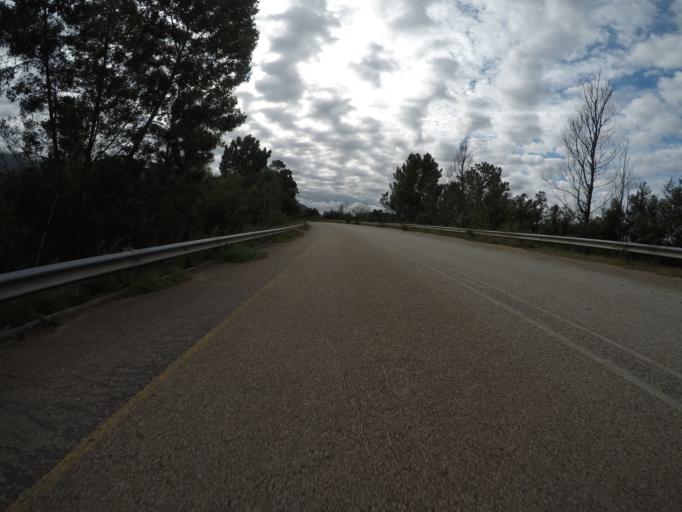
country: ZA
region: Eastern Cape
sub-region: Cacadu District Municipality
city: Kareedouw
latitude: -34.0149
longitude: 24.3047
